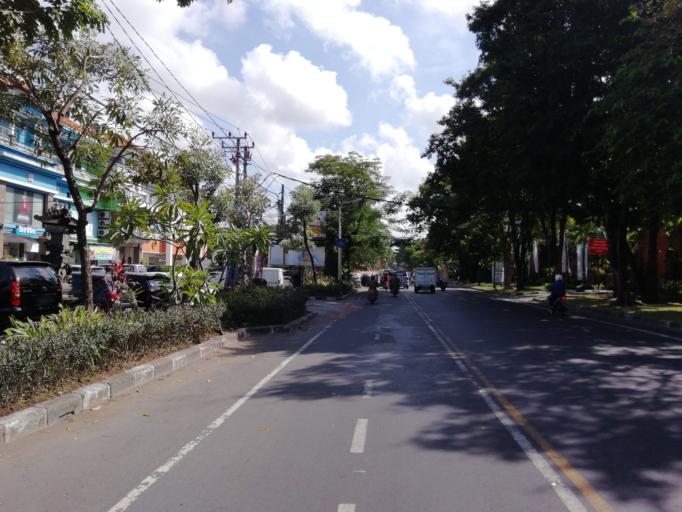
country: ID
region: Bali
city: Denpasar
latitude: -8.6707
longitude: 115.2217
